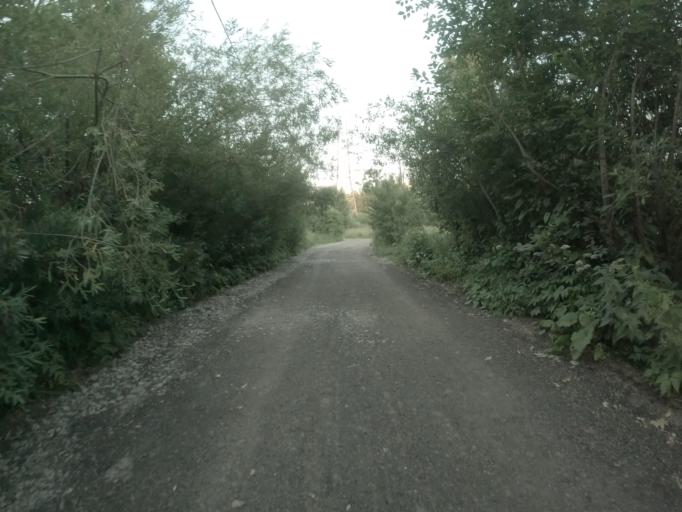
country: RU
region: St.-Petersburg
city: Krasnogvargeisky
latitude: 59.9532
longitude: 30.5073
